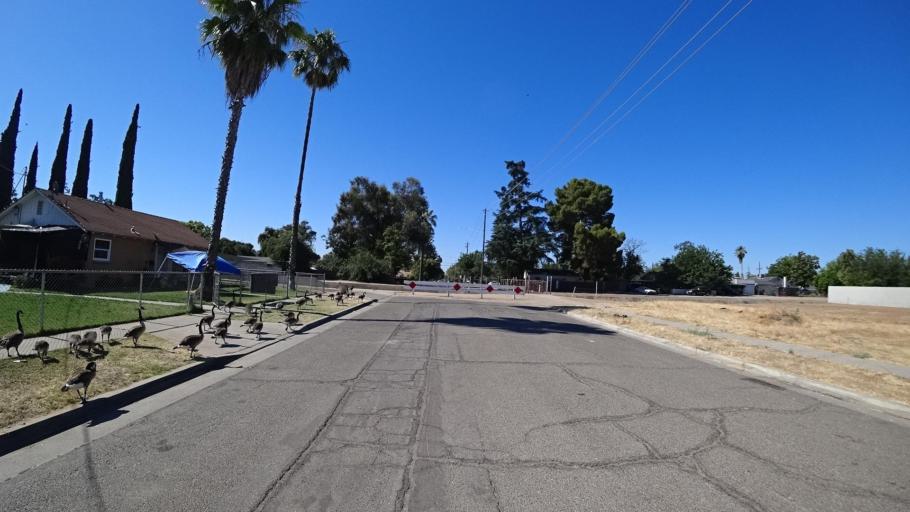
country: US
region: California
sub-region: Fresno County
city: Fresno
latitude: 36.7835
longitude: -119.7951
